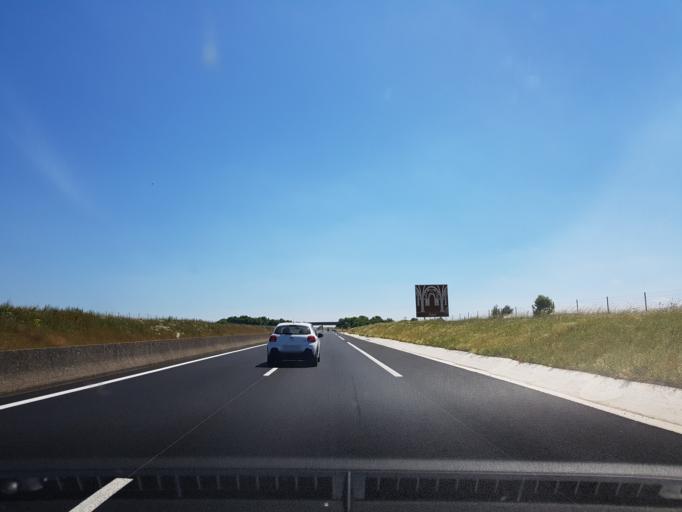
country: FR
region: Picardie
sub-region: Departement de la Somme
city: Nesle
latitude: 49.8355
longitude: 2.9390
